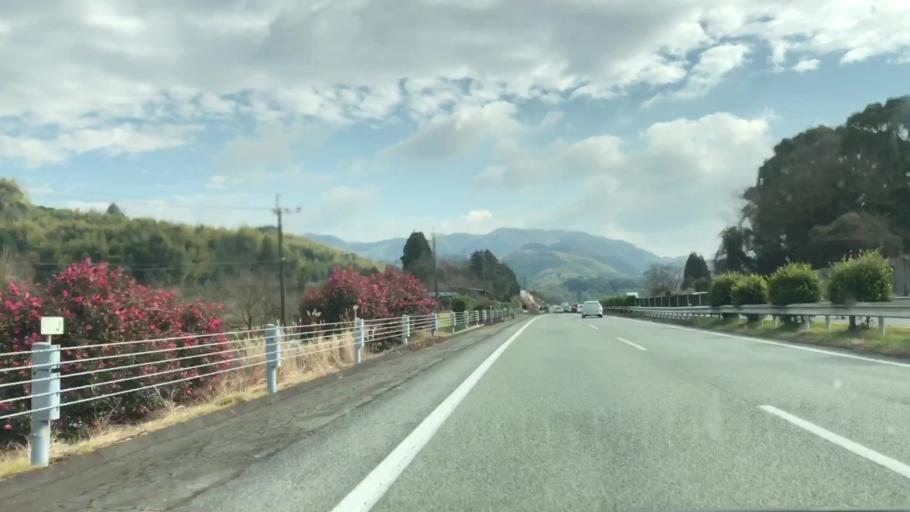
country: JP
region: Fukuoka
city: Setakamachi-takayanagi
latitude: 33.1183
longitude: 130.5248
